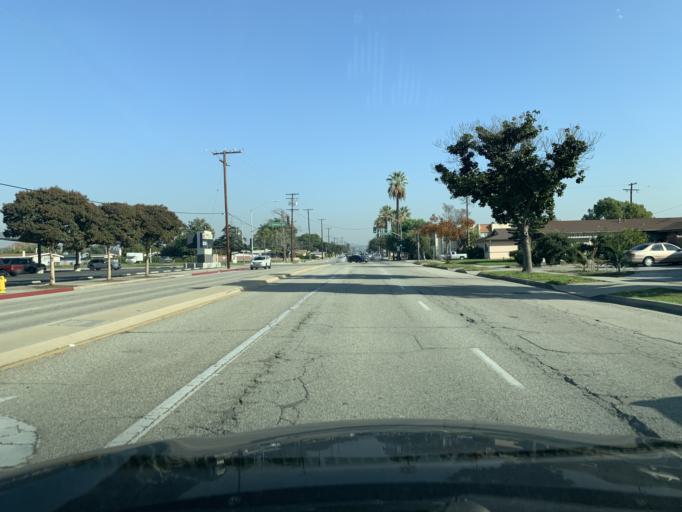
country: US
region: California
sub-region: Los Angeles County
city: Covina
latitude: 34.0791
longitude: -117.9000
